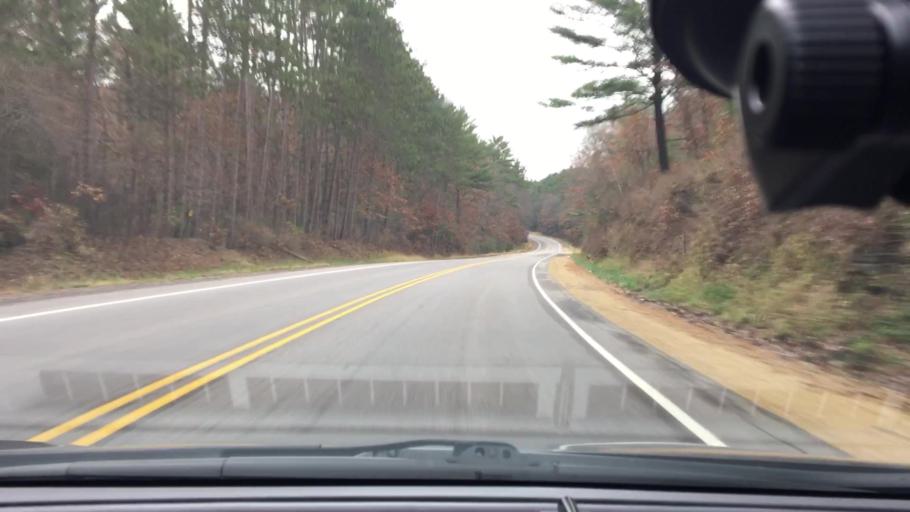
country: US
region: Wisconsin
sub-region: Columbia County
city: Wisconsin Dells
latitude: 43.6470
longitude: -89.8072
